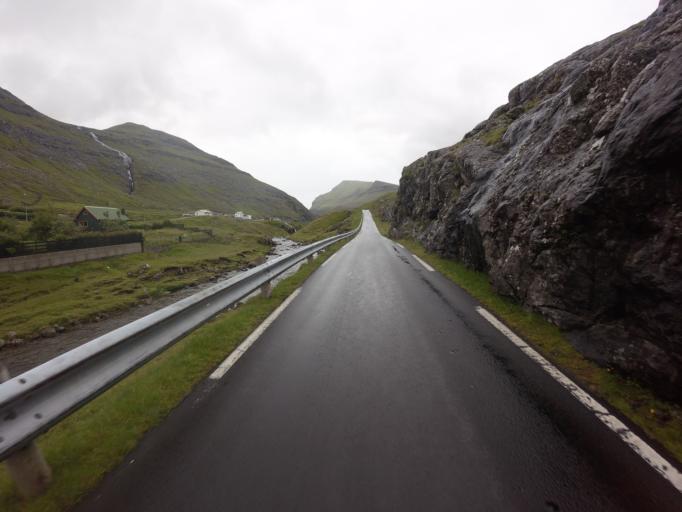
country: FO
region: Streymoy
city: Vestmanna
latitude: 62.2422
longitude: -7.1614
